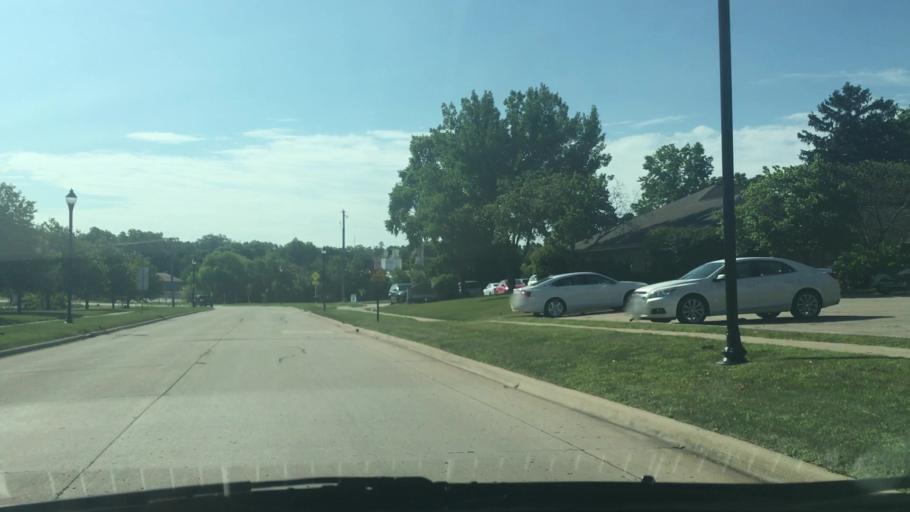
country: US
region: Iowa
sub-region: Johnson County
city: North Liberty
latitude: 41.7492
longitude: -91.6061
